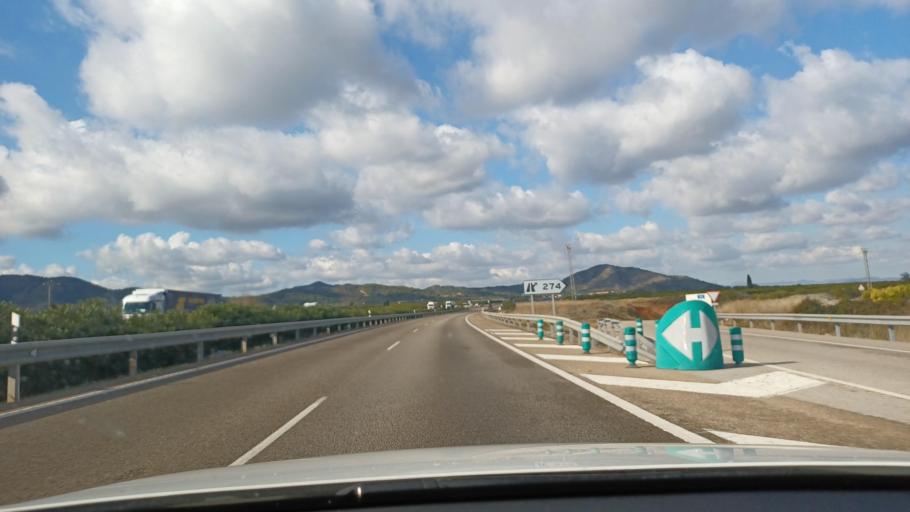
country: ES
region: Valencia
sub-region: Provincia de Castello
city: Villavieja
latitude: 39.8738
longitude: -0.1889
